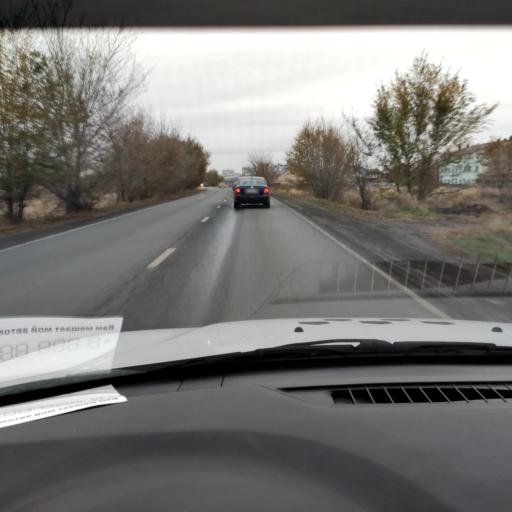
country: RU
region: Samara
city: Podstepki
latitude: 53.5151
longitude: 49.2391
